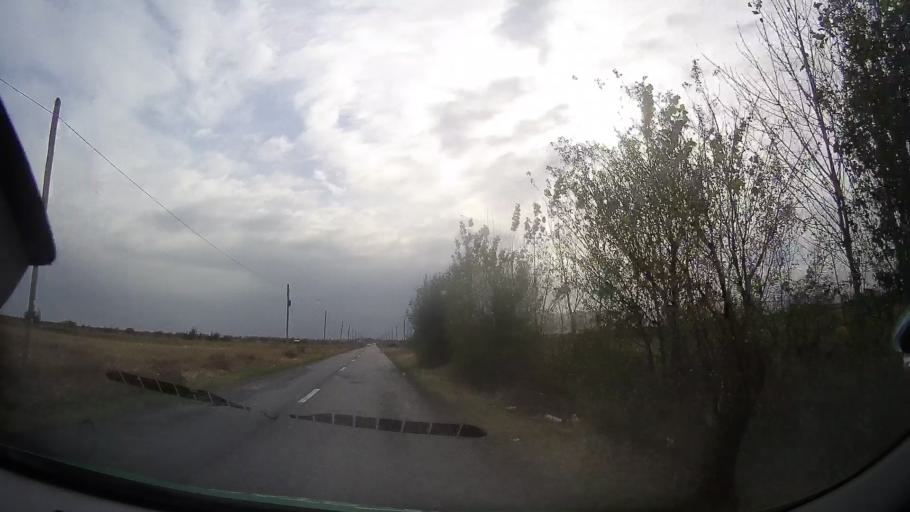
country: RO
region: Ialomita
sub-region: Comuna Fierbinti-Targ
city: Fierbintii de Jos
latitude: 44.7115
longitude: 26.3911
